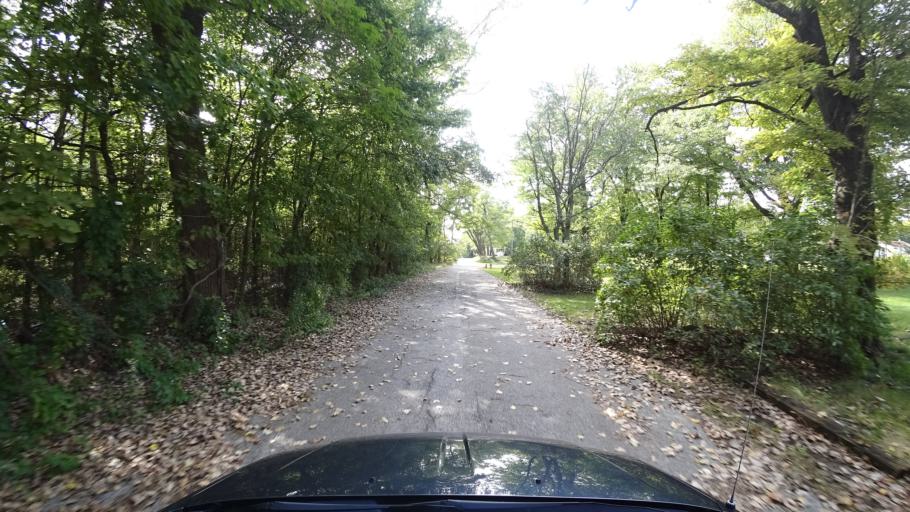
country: US
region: Indiana
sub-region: LaPorte County
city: Michigan City
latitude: 41.7213
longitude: -86.8865
